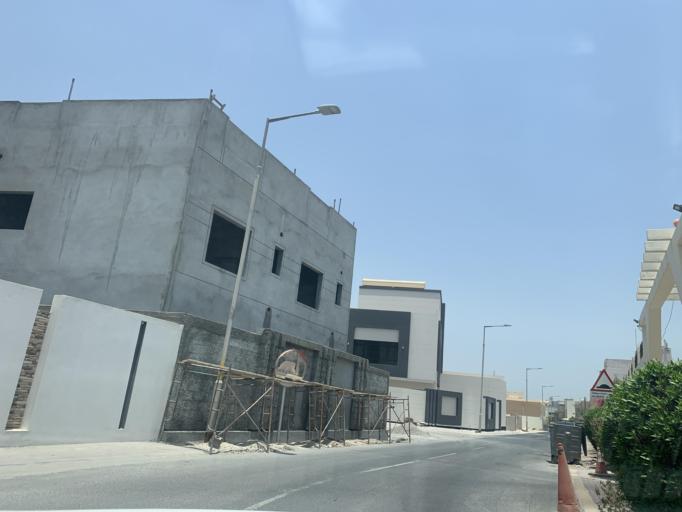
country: BH
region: Manama
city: Jidd Hafs
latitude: 26.2073
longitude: 50.4726
